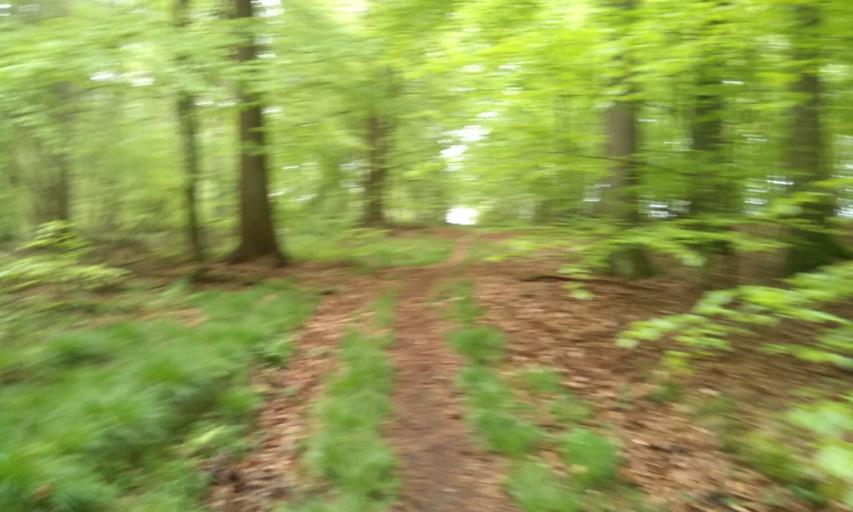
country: DE
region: Lower Saxony
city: Buxtehude
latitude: 53.4672
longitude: 9.6486
